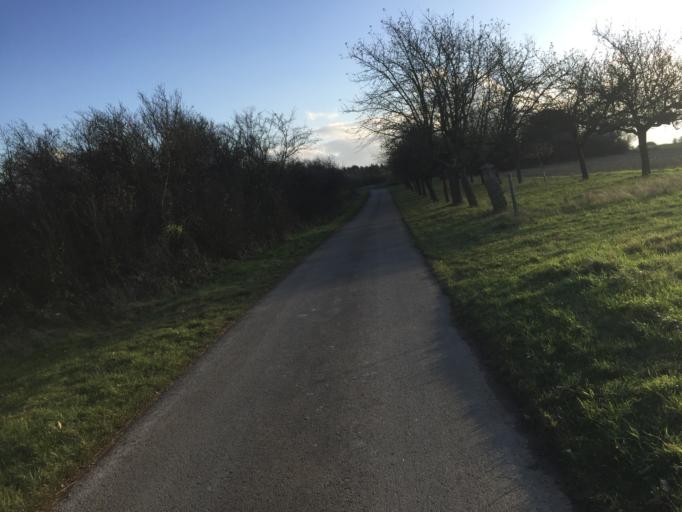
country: DE
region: Hesse
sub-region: Regierungsbezirk Giessen
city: Langgons
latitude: 50.5201
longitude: 8.7118
